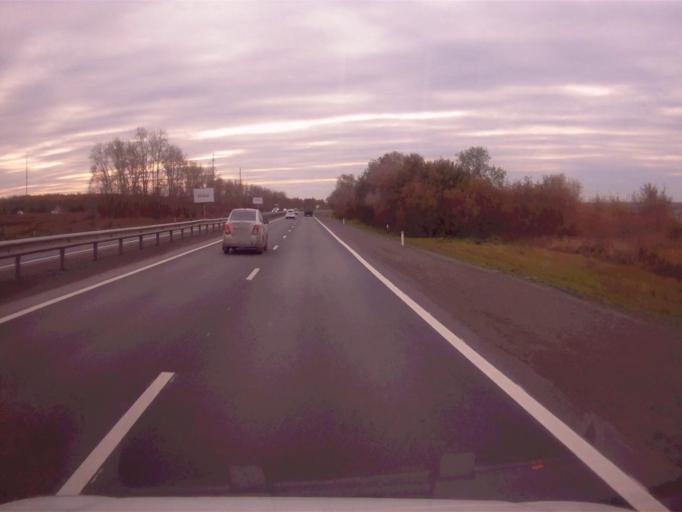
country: RU
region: Chelyabinsk
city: Roza
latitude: 54.9866
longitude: 61.4356
